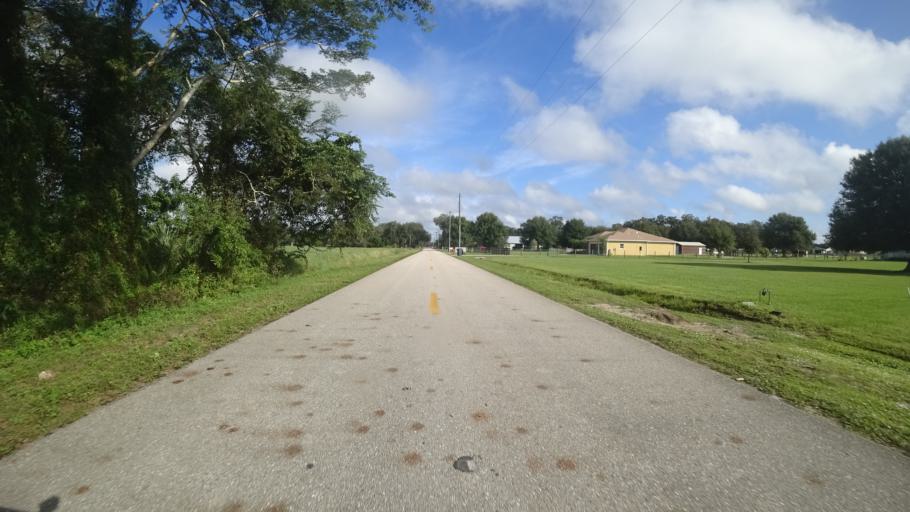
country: US
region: Florida
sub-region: Manatee County
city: Ellenton
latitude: 27.5700
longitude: -82.4089
